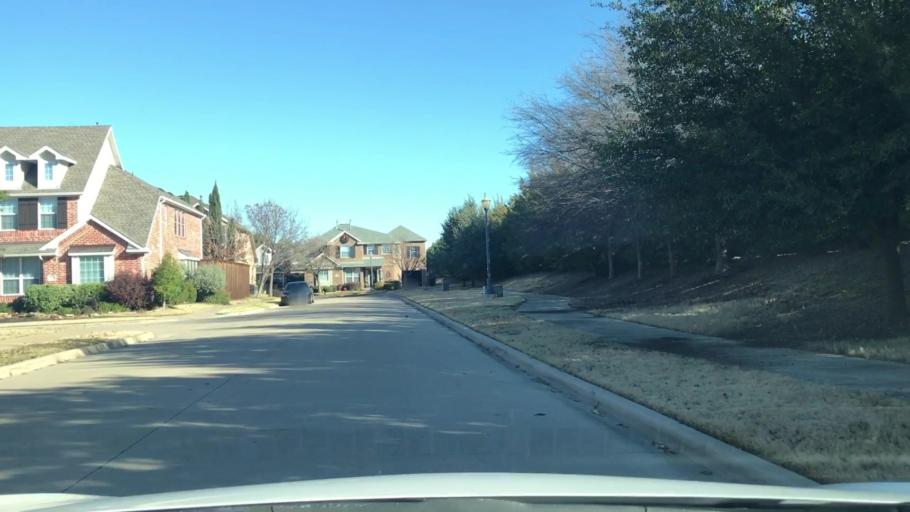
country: US
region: Texas
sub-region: Collin County
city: Frisco
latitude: 33.1158
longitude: -96.8485
